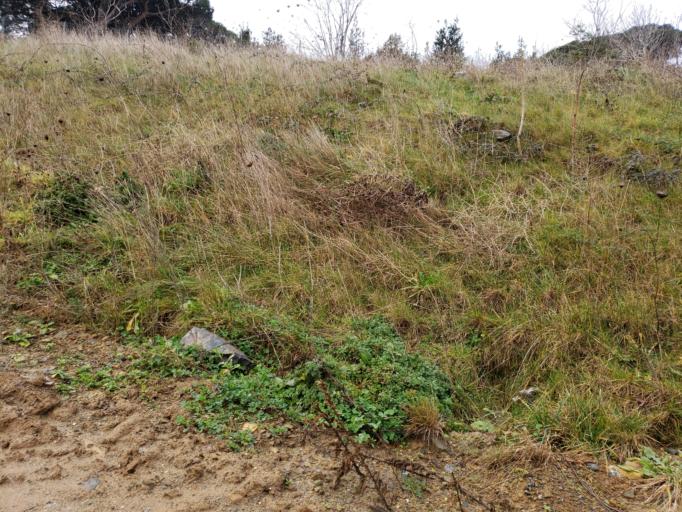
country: TR
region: Istanbul
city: Arikoey
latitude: 41.1677
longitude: 29.0539
